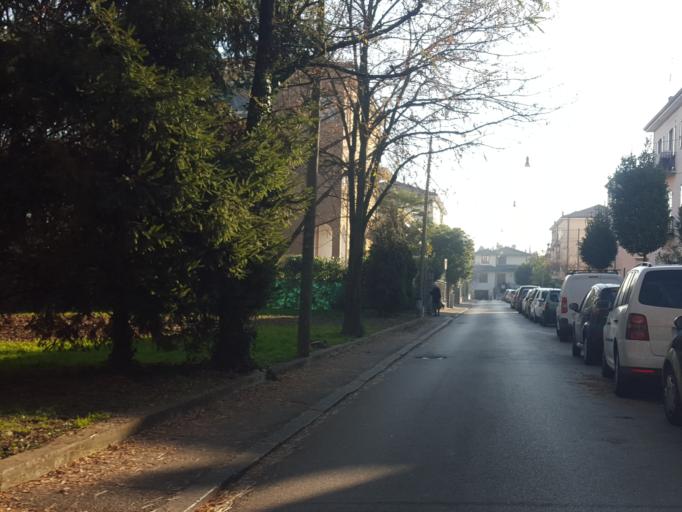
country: IT
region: Veneto
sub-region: Provincia di Vicenza
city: Vicenza
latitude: 45.5546
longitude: 11.5585
